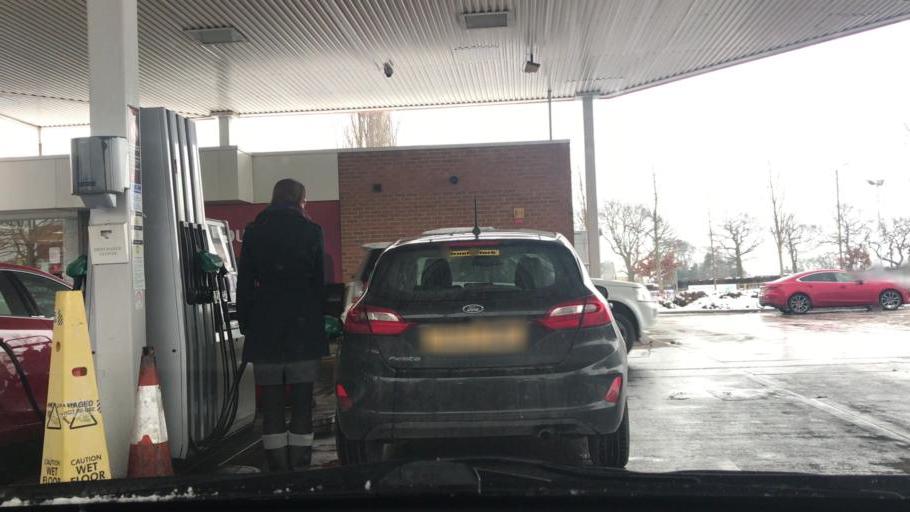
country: GB
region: England
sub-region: North Yorkshire
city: Knaresborough
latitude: 53.9857
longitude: -1.4978
